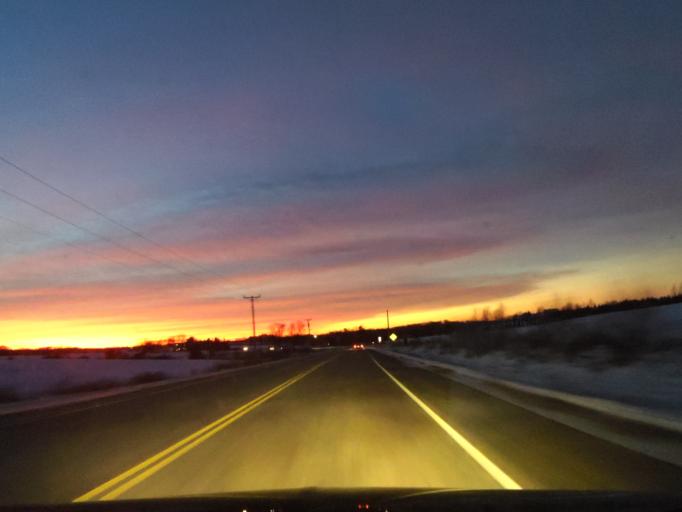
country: US
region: Minnesota
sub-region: Chisago County
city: Lindstrom
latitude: 45.3486
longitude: -92.8317
